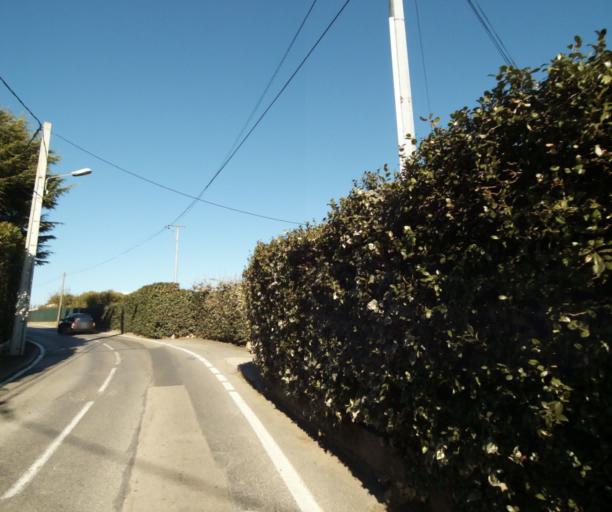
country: FR
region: Provence-Alpes-Cote d'Azur
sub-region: Departement des Alpes-Maritimes
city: Biot
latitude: 43.6067
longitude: 7.0890
